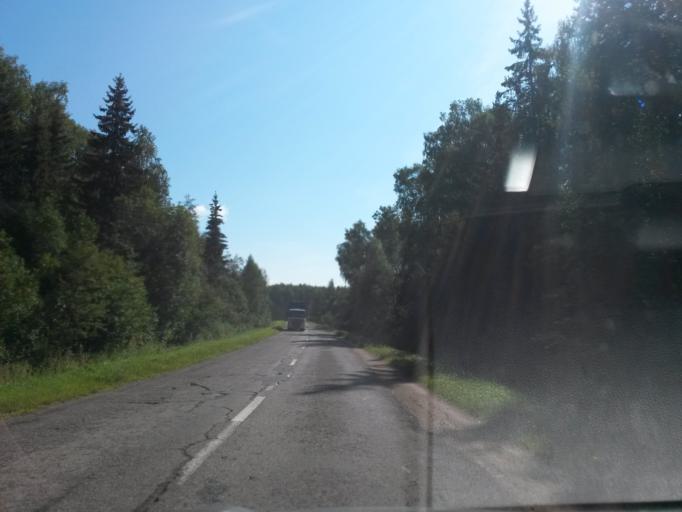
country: RU
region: Jaroslavl
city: Dubki
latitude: 57.2900
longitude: 40.1054
